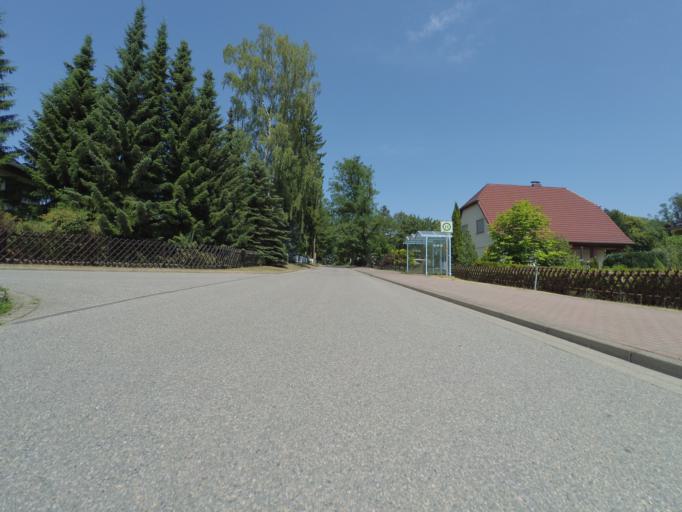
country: DE
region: Mecklenburg-Vorpommern
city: Plau am See
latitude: 53.4378
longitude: 12.2850
